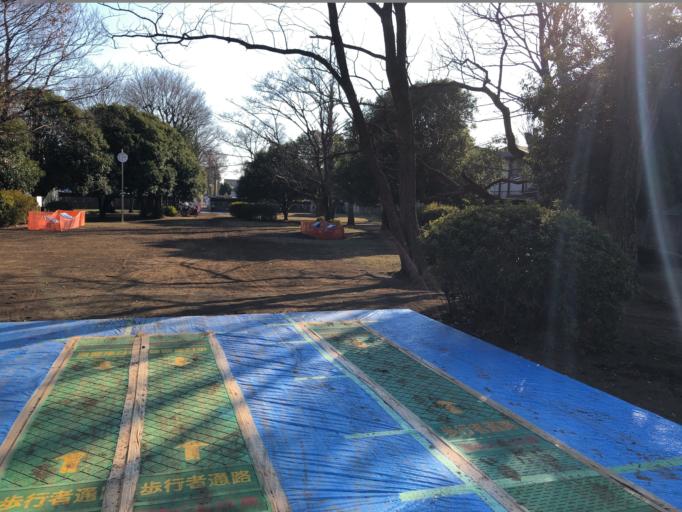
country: JP
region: Tokyo
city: Mitaka-shi
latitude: 35.6846
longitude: 139.5396
